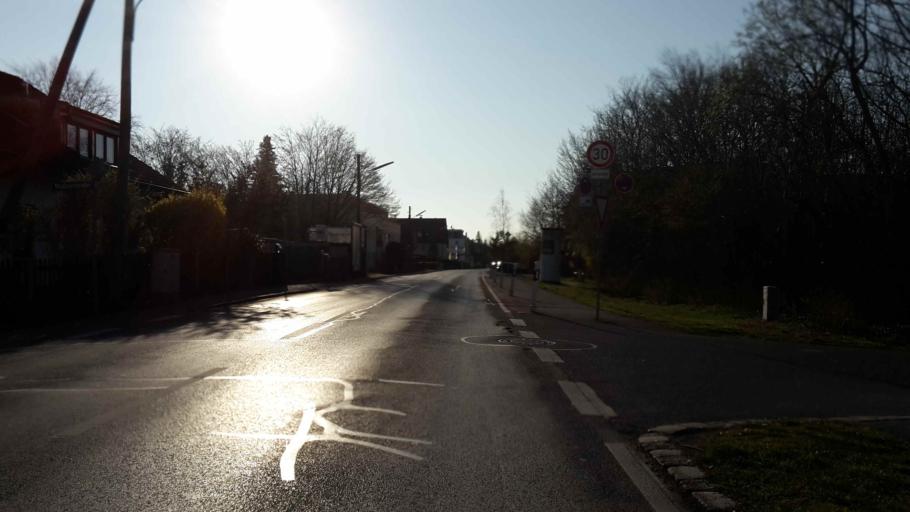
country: DE
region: Bavaria
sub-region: Upper Bavaria
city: Karlsfeld
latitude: 48.1804
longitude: 11.4820
